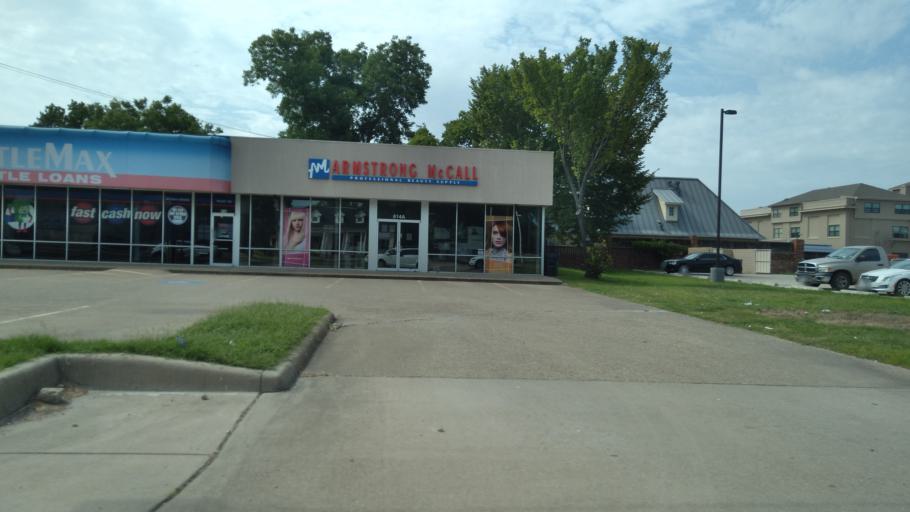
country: US
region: Texas
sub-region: Navarro County
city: Corsicana
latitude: 32.0889
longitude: -96.4691
